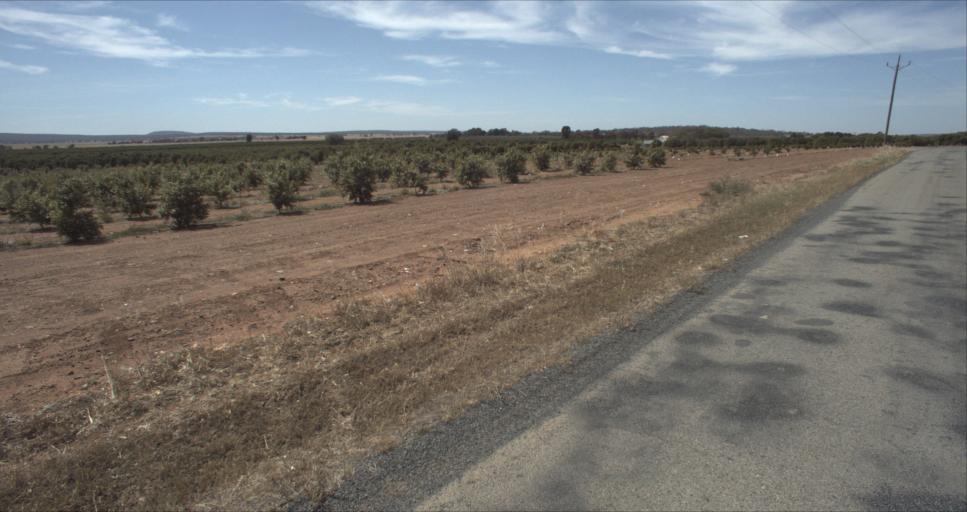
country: AU
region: New South Wales
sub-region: Leeton
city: Leeton
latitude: -34.5673
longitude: 146.4637
